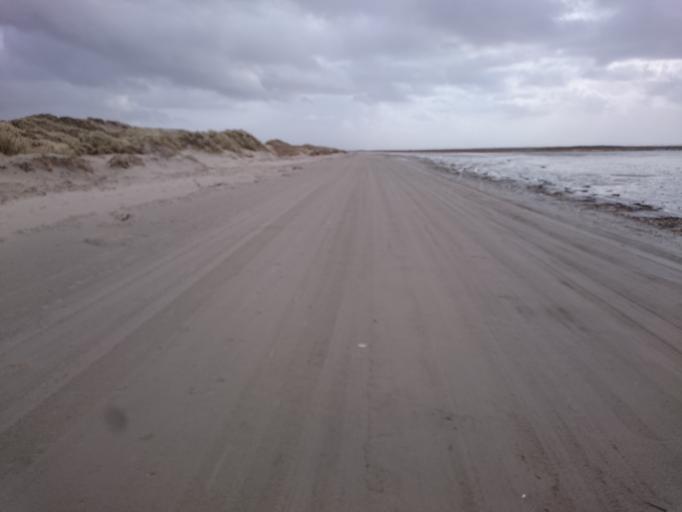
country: DK
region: South Denmark
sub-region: Fano Kommune
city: Nordby
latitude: 55.4301
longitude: 8.3657
